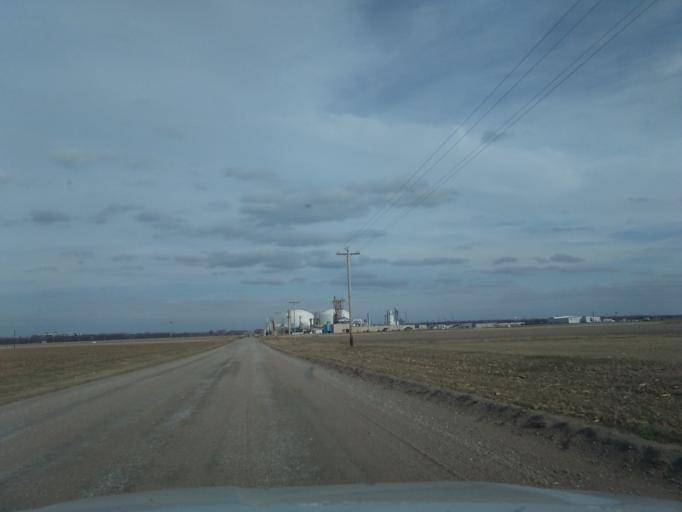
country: US
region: Nebraska
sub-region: Gage County
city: Beatrice
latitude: 40.3210
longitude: -96.8499
